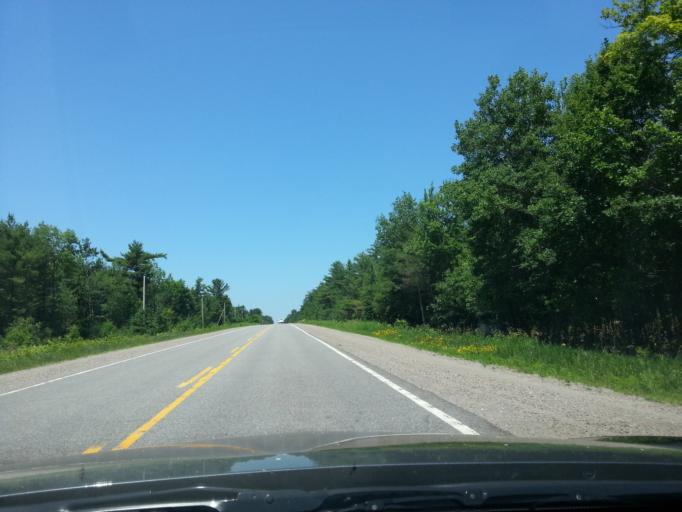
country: CA
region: Ontario
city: Arnprior
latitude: 45.5279
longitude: -76.3023
